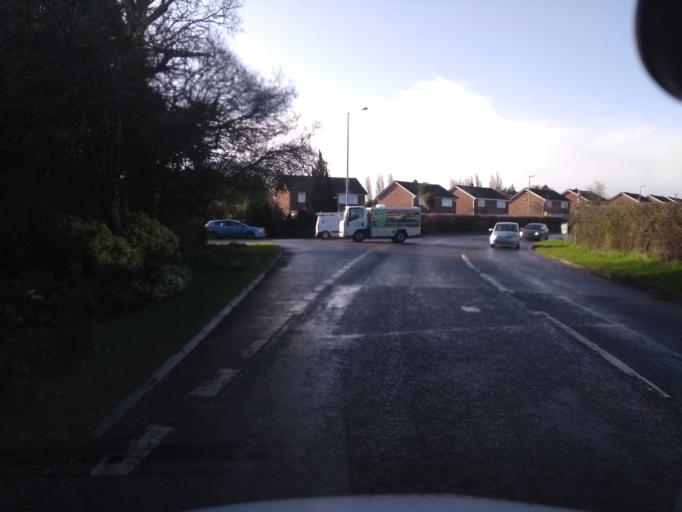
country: GB
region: England
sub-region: Somerset
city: Yeovil
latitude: 50.9604
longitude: -2.6214
